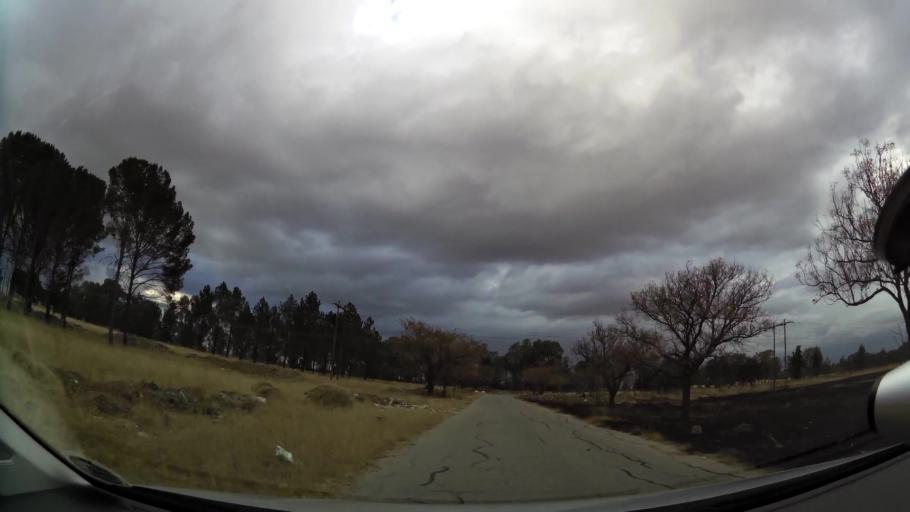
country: ZA
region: Orange Free State
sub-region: Lejweleputswa District Municipality
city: Welkom
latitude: -27.9658
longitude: 26.7030
